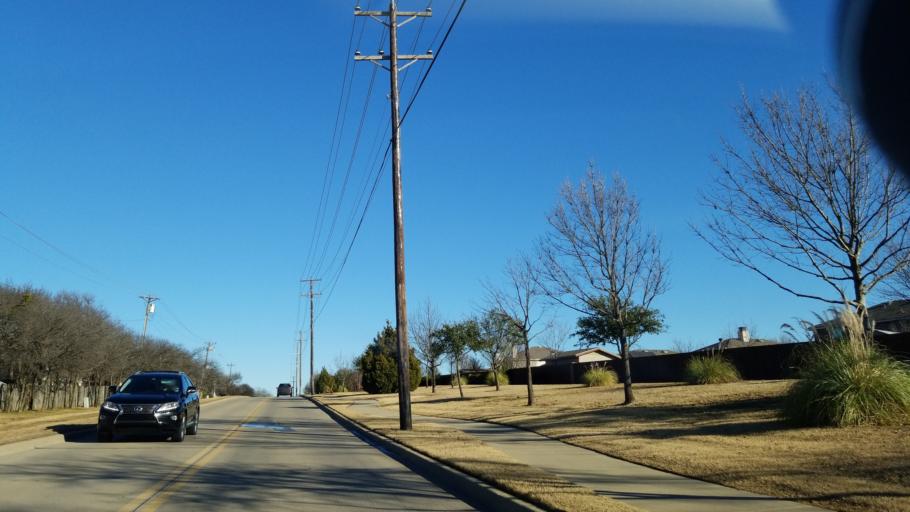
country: US
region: Texas
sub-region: Denton County
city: Corinth
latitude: 33.1583
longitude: -97.1012
